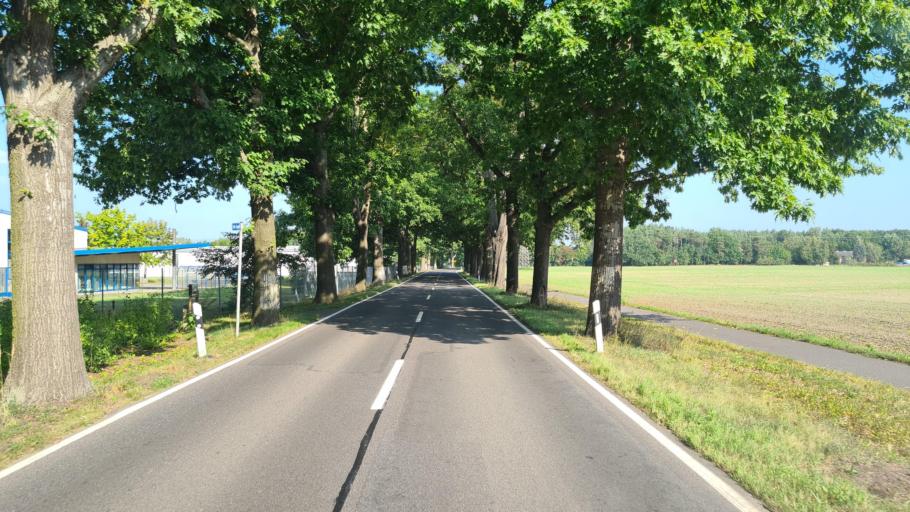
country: DE
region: Brandenburg
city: Kolkwitz
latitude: 51.7361
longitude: 14.2600
